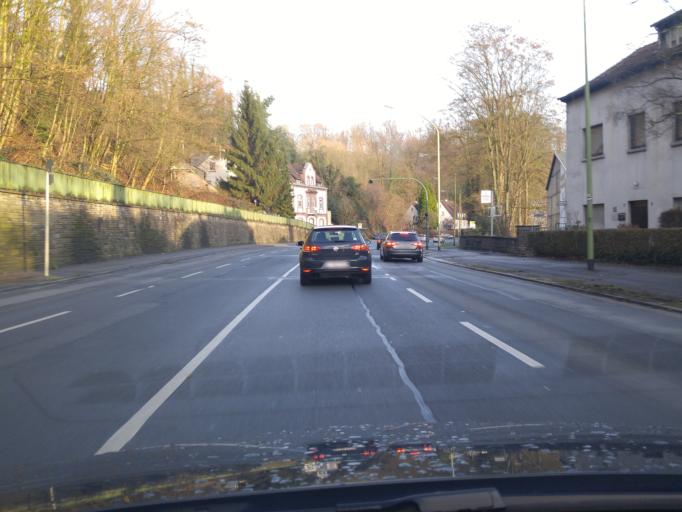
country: DE
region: North Rhine-Westphalia
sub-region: Regierungsbezirk Dusseldorf
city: Essen
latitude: 51.4374
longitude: 7.0593
